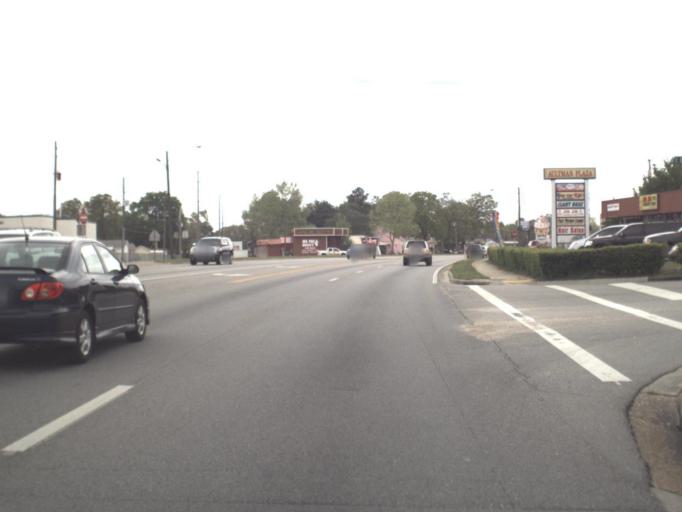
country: US
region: Florida
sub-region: Okaloosa County
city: Crestview
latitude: 30.7544
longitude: -86.5648
